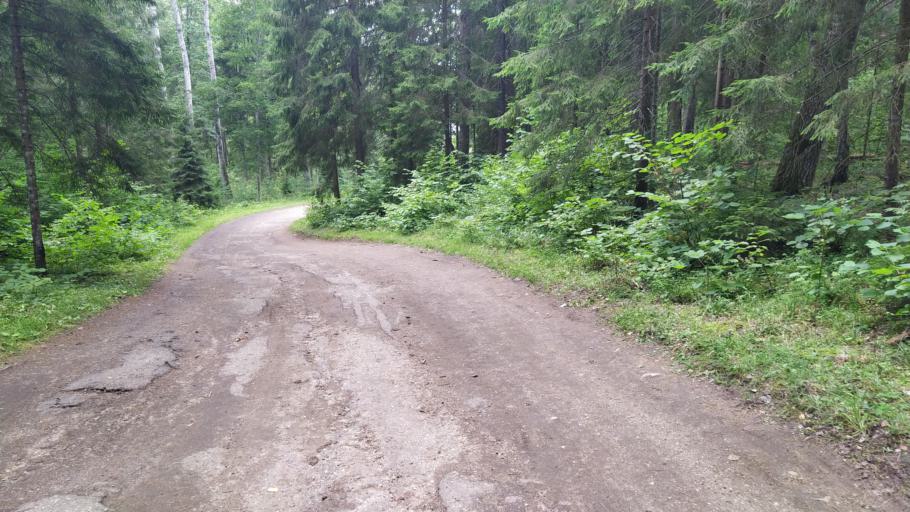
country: RU
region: Pskov
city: Pushkinskiye Gory
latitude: 57.0587
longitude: 28.9384
